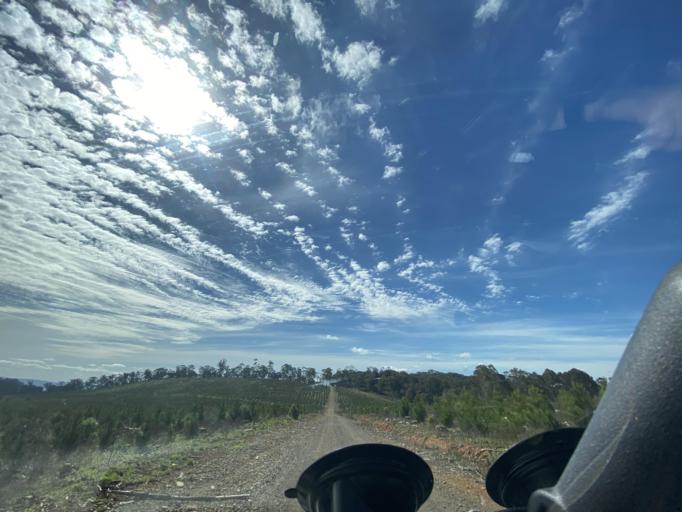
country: AU
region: Victoria
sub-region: Mansfield
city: Mansfield
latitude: -36.8219
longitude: 146.1030
